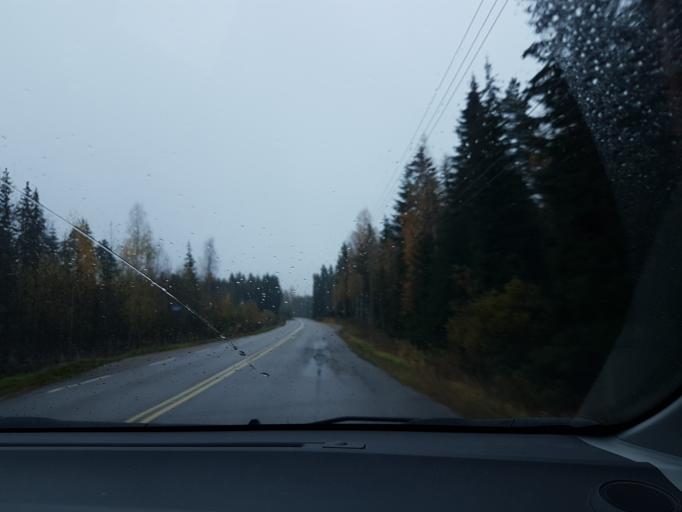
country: FI
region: Uusimaa
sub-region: Helsinki
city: Jaervenpaeae
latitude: 60.5793
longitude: 25.1621
